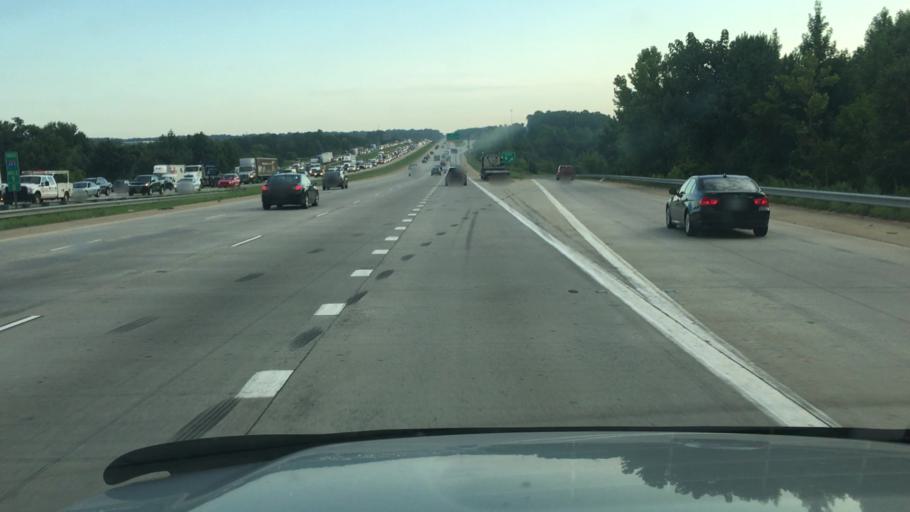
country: US
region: North Carolina
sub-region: Gaston County
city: Belmont
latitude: 35.2314
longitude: -80.9704
